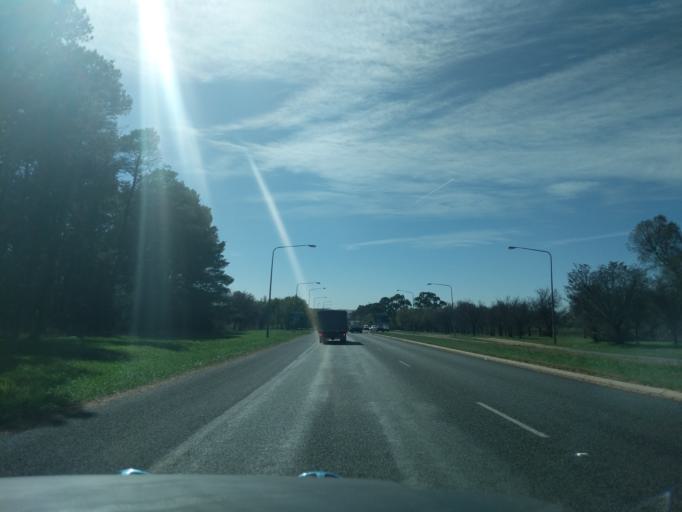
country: AU
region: Australian Capital Territory
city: Forrest
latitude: -35.3439
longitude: 149.1515
